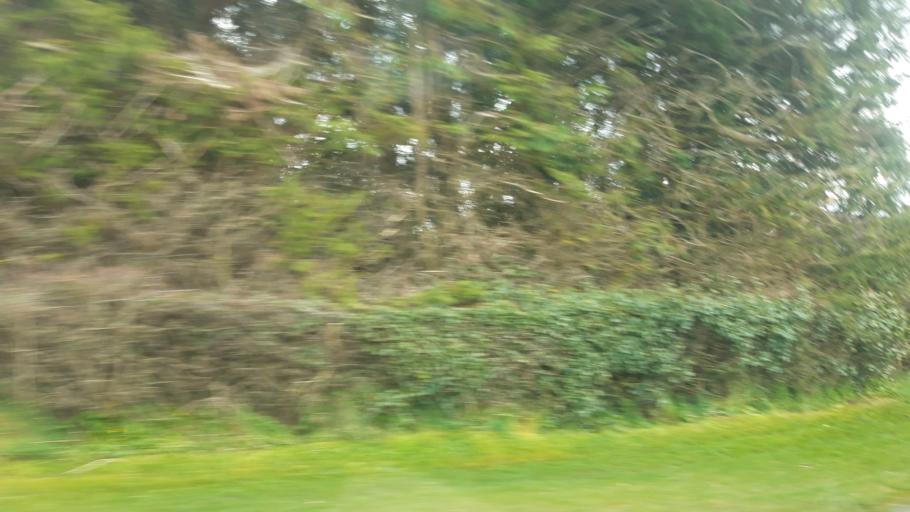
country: IE
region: Leinster
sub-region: Kildare
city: Clane
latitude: 53.3025
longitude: -6.7007
